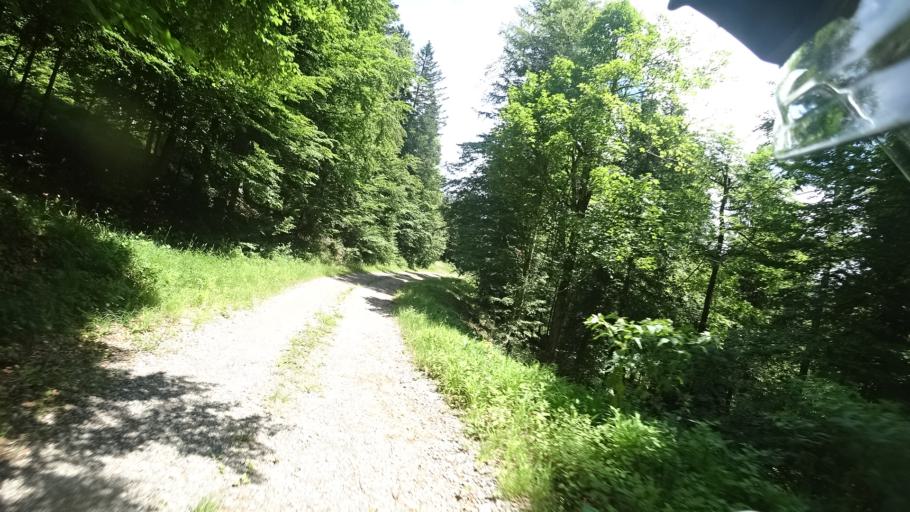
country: SI
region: Loska Dolina
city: Leskova Dolina
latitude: 45.5642
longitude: 14.5696
